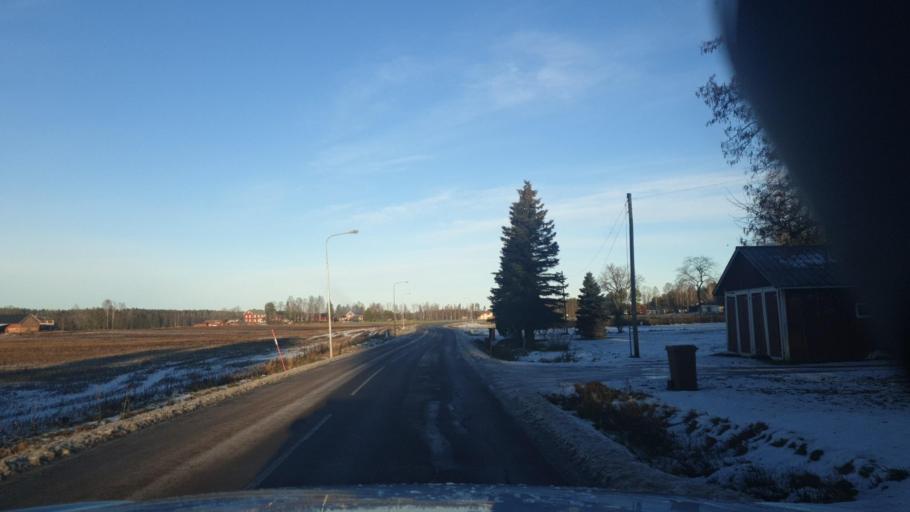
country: SE
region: Vaermland
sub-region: Arvika Kommun
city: Arvika
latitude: 59.5656
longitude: 12.5560
